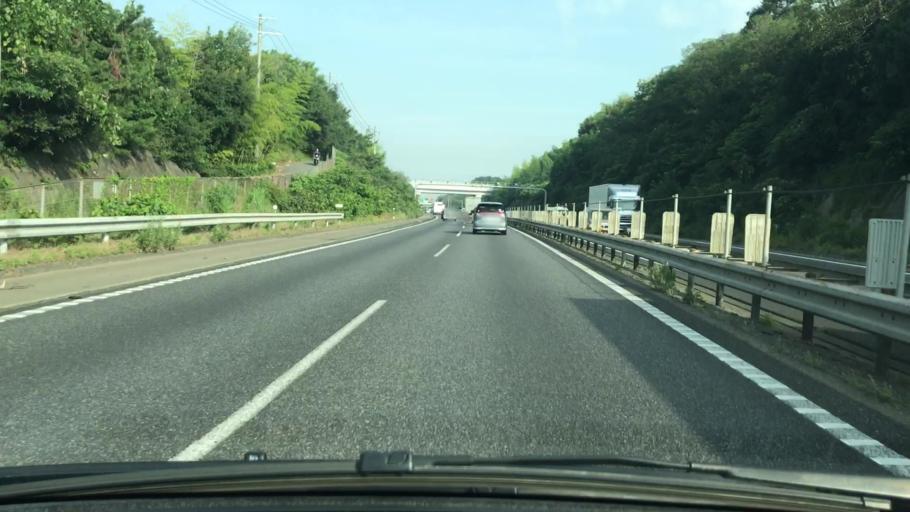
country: JP
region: Hyogo
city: Akashi
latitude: 34.7000
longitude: 134.9641
